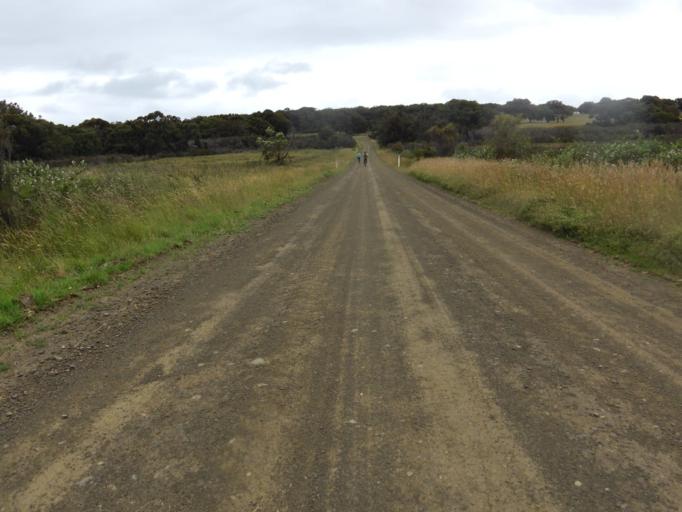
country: AU
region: Victoria
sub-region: Bass Coast
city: Cowes
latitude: -38.3872
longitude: 145.3865
